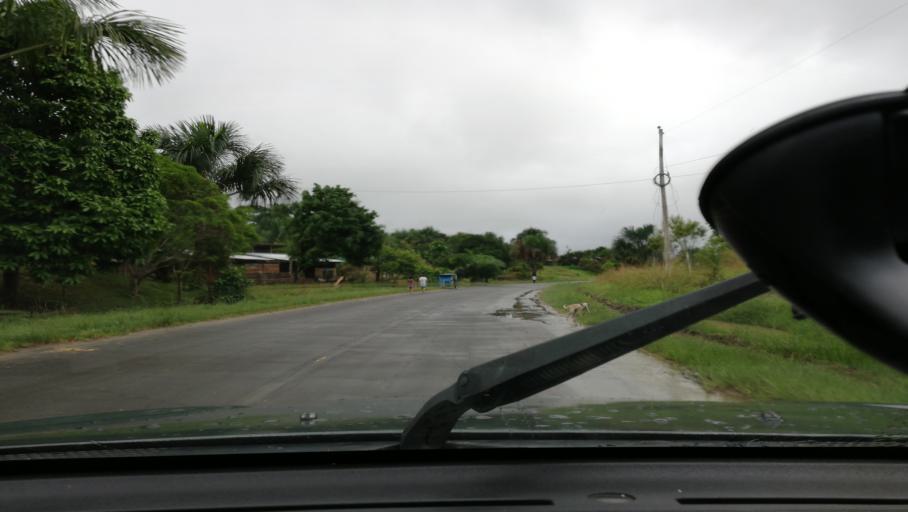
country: PE
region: Loreto
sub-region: Provincia de Loreto
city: Nauta
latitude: -4.2350
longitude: -73.4883
